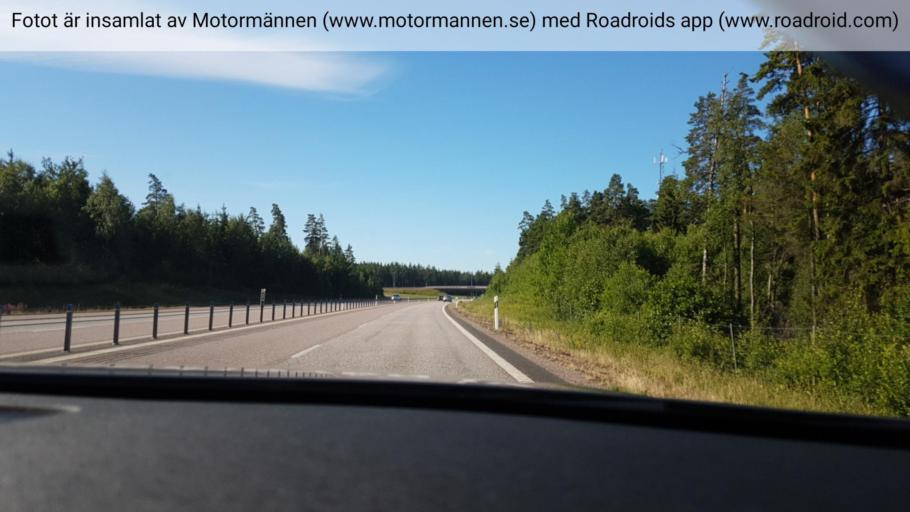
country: SE
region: Vaestra Goetaland
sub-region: Skovde Kommun
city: Skultorp
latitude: 58.3443
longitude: 13.8651
